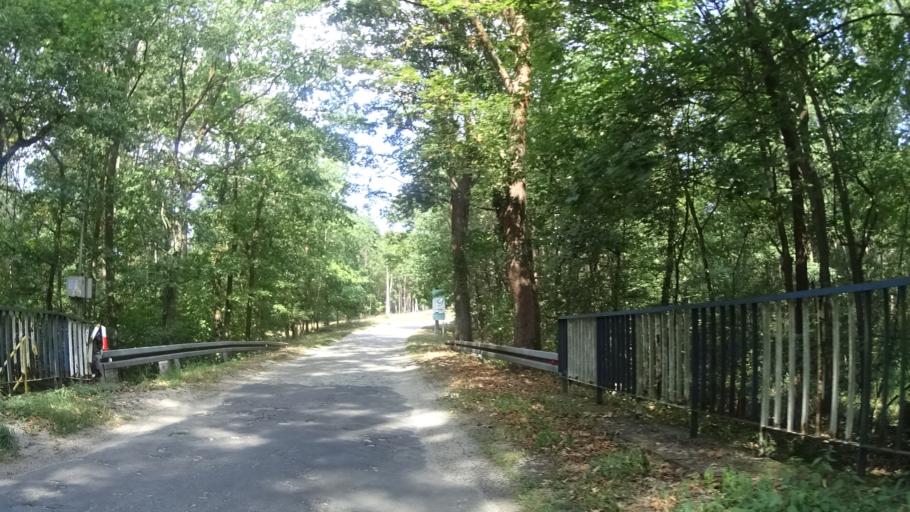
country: PL
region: Lubusz
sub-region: Powiat zarski
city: Leknica
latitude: 51.5252
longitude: 14.8215
